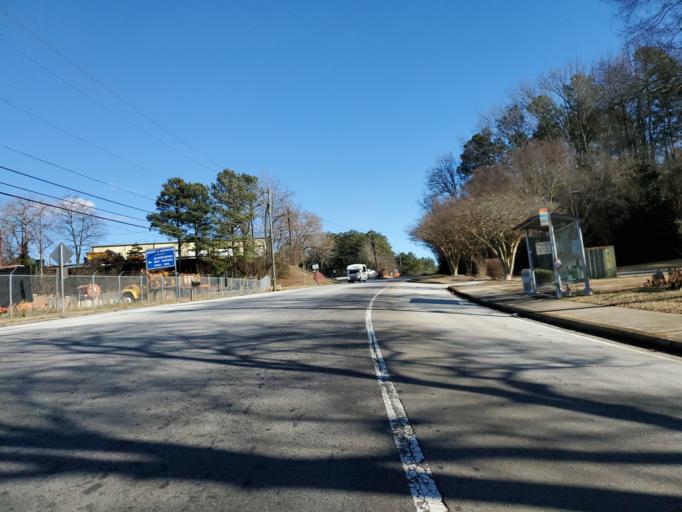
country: US
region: Georgia
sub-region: DeKalb County
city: Avondale Estates
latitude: 33.7715
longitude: -84.2388
